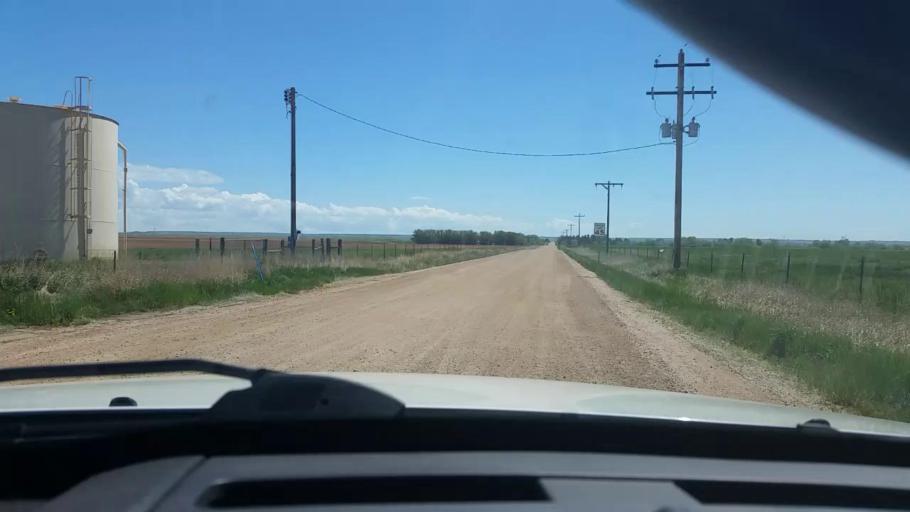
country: US
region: Colorado
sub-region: Larimer County
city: Wellington
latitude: 40.7982
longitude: -105.0759
